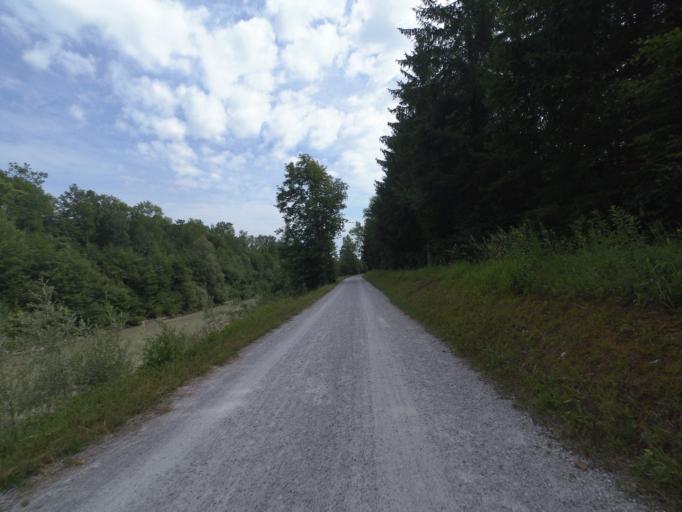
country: DE
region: Bavaria
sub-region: Upper Bavaria
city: Ainring
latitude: 47.8002
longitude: 12.9649
